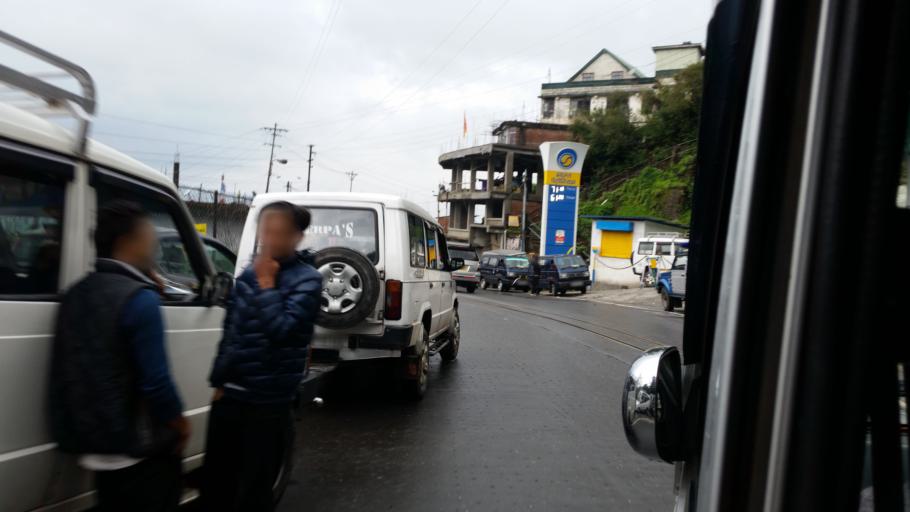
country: IN
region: West Bengal
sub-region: Darjiling
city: Darjiling
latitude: 27.0238
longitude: 88.2538
